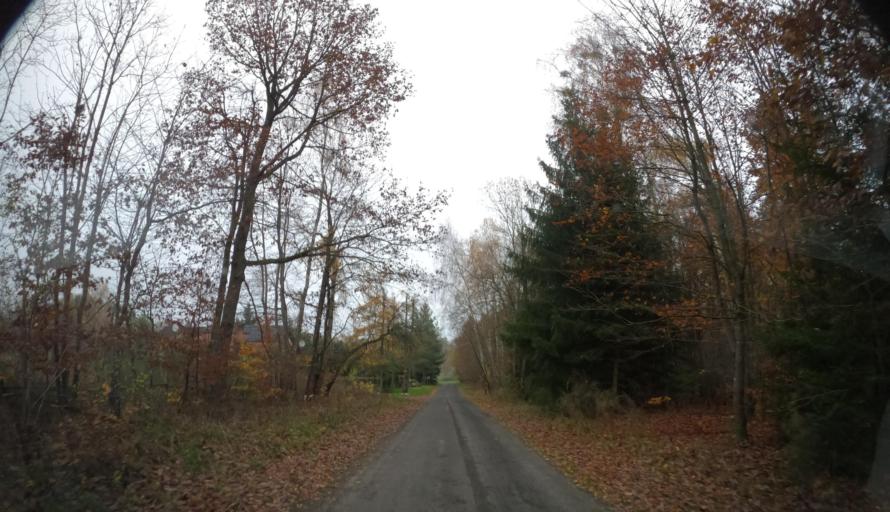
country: PL
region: West Pomeranian Voivodeship
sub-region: Powiat lobeski
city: Radowo Male
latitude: 53.6811
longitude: 15.4541
